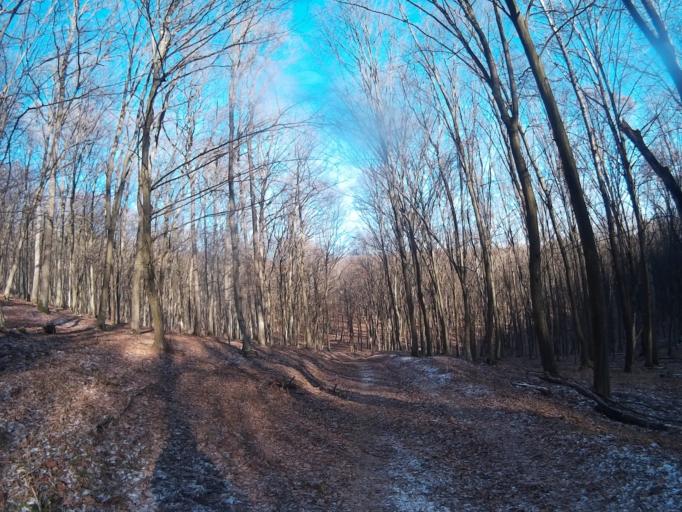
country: HU
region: Borsod-Abauj-Zemplen
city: Rudabanya
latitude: 48.4980
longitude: 20.5889
